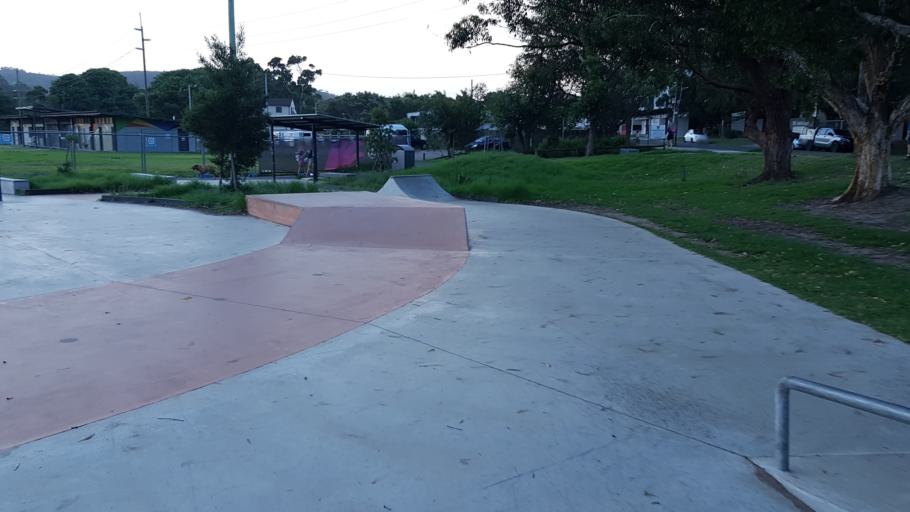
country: AU
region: New South Wales
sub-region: Warringah
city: Narraweena
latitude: -33.7345
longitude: 151.2794
